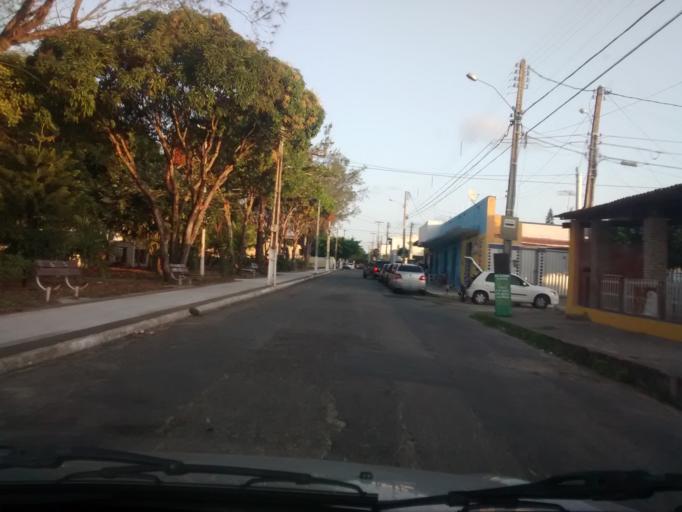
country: BR
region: Rio Grande do Norte
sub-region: Natal
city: Natal
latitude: -5.8723
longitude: -35.1868
